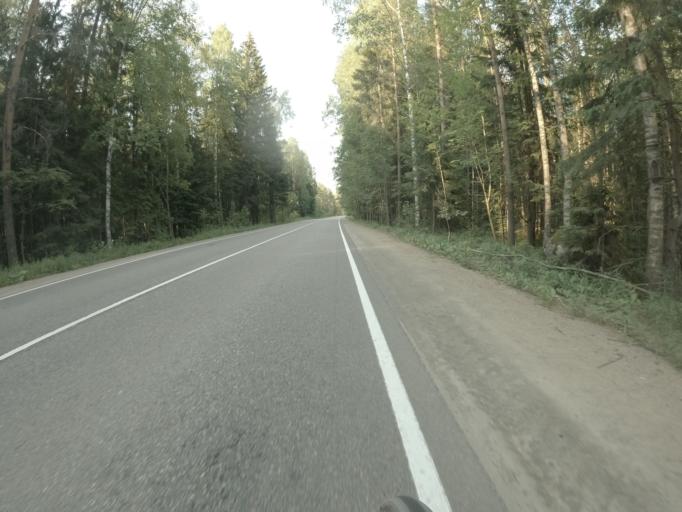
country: RU
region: Leningrad
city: Veshchevo
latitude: 60.4658
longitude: 29.2443
